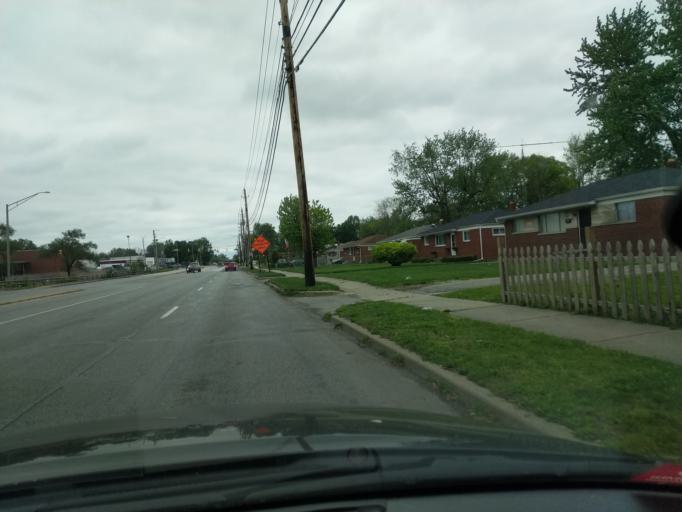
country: US
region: Indiana
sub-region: Marion County
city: Lawrence
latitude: 39.8273
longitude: -86.0649
